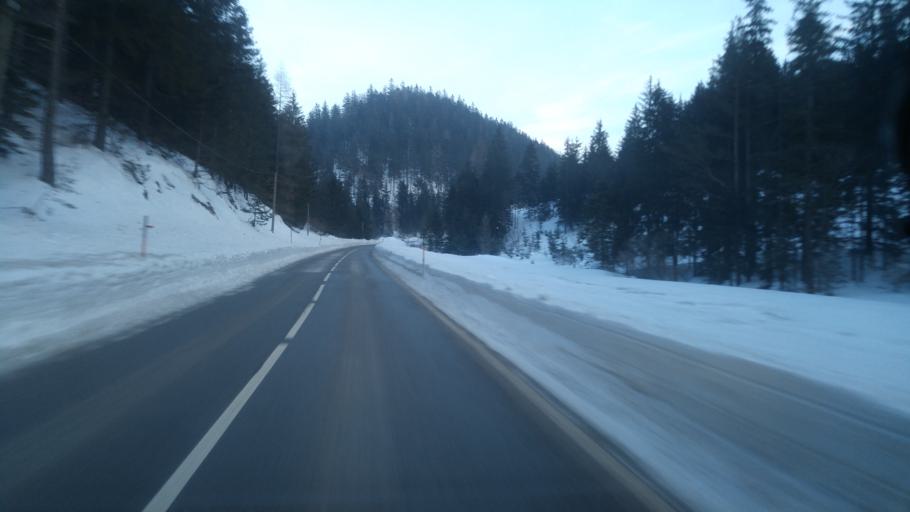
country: AT
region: Lower Austria
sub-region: Politischer Bezirk Wiener Neustadt
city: Rohr im Gebirge
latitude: 47.8725
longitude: 15.7851
